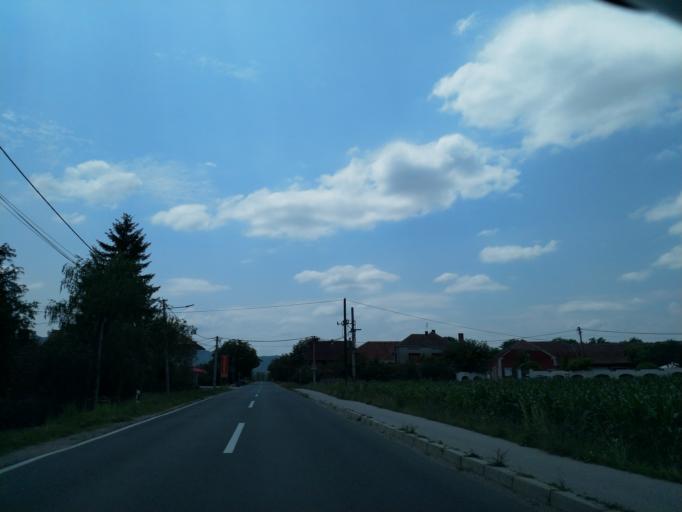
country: RS
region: Central Serbia
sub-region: Toplicki Okrug
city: Blace
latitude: 43.4452
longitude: 21.2293
